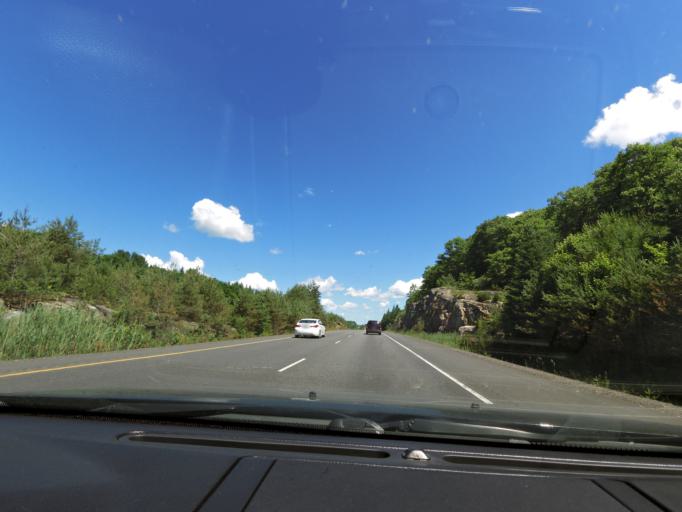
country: CA
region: Ontario
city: Bracebridge
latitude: 45.1724
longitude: -79.3116
